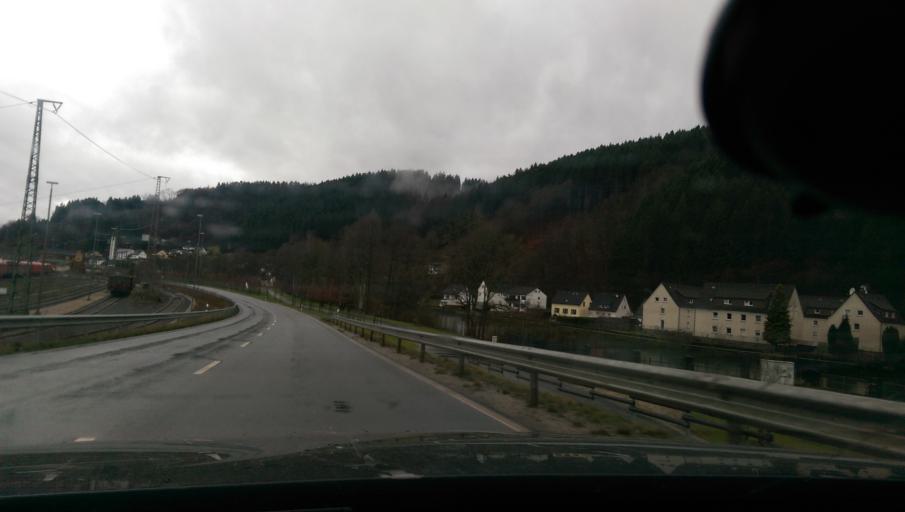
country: DE
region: North Rhine-Westphalia
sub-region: Regierungsbezirk Arnsberg
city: Finnentrop
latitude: 51.1789
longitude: 7.9673
